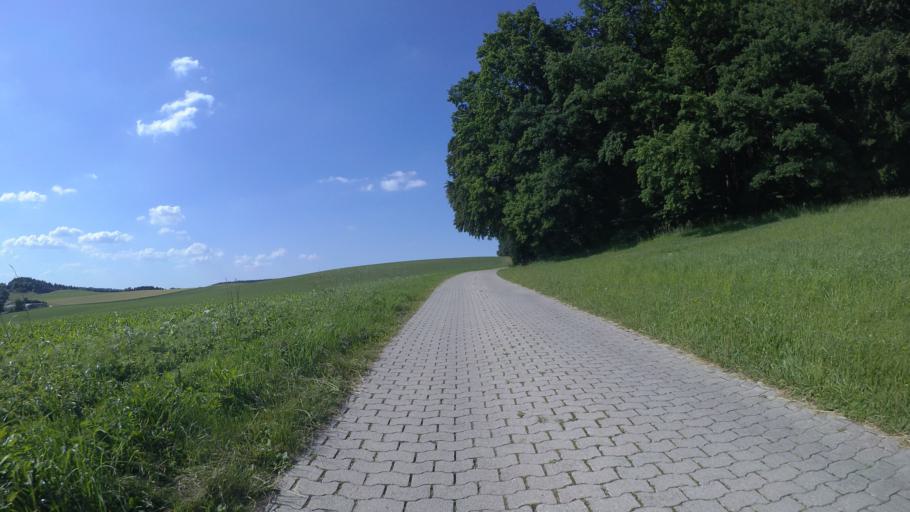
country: DE
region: Bavaria
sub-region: Upper Bavaria
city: Seeon-Seebruck
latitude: 47.9661
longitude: 12.4989
